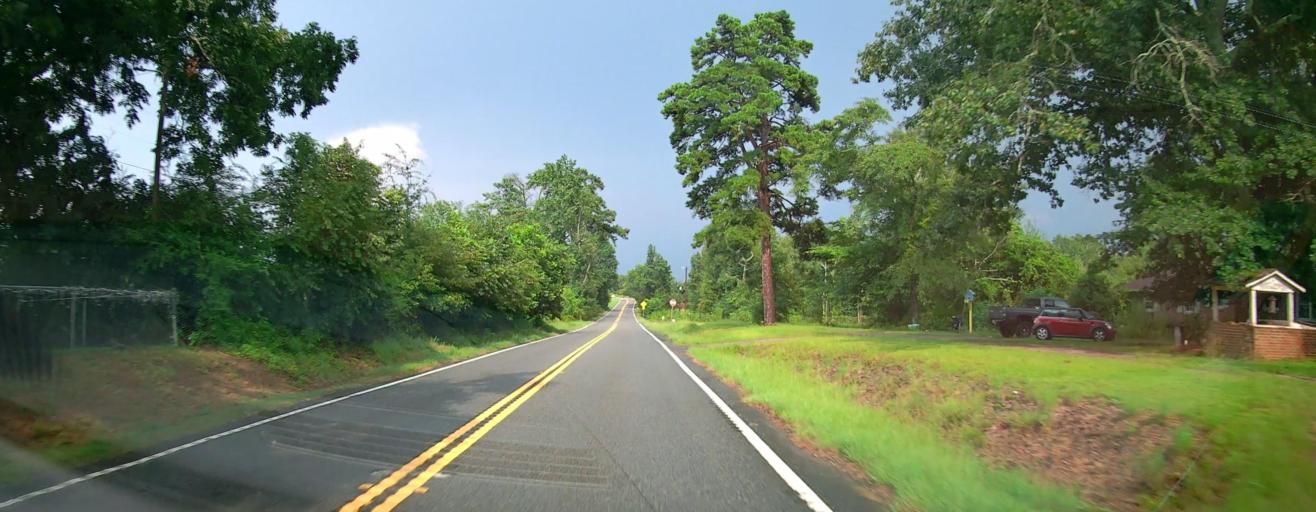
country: US
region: Georgia
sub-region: Twiggs County
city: Jeffersonville
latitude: 32.6061
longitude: -83.2799
